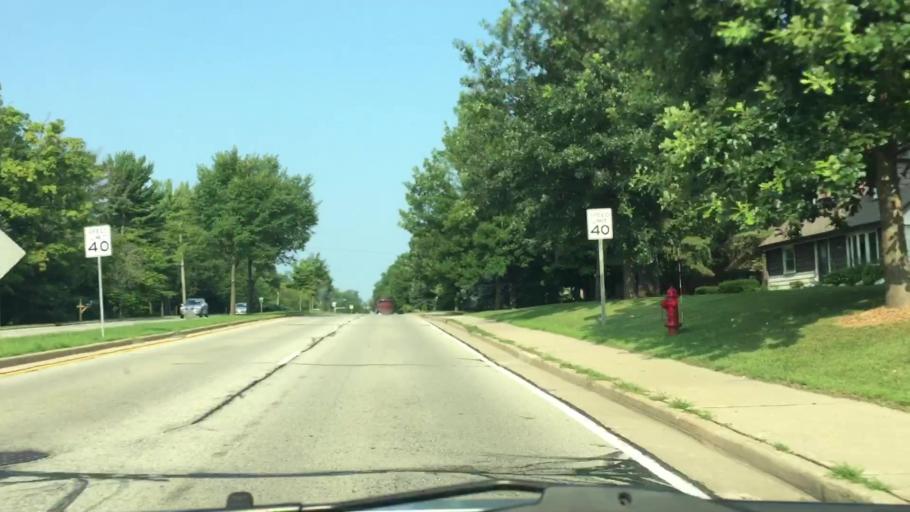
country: US
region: Wisconsin
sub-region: Waukesha County
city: Elm Grove
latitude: 43.0165
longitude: -88.0710
